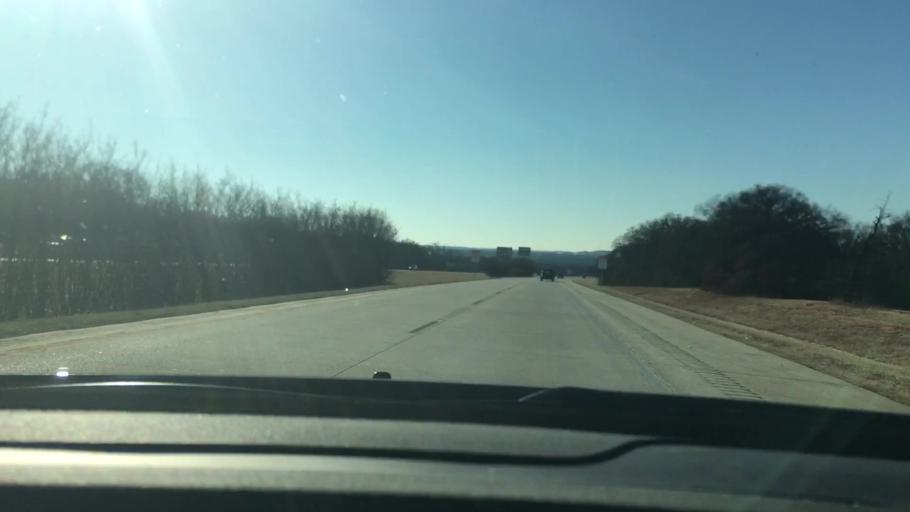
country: US
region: Oklahoma
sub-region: Carter County
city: Ardmore
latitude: 34.0612
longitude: -97.1496
